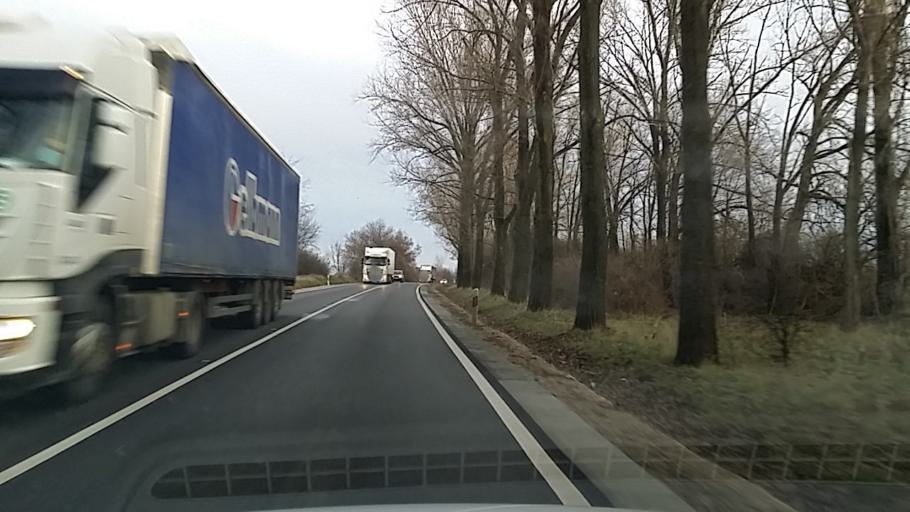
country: HU
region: Fejer
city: Bodajk
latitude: 47.3326
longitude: 18.2588
